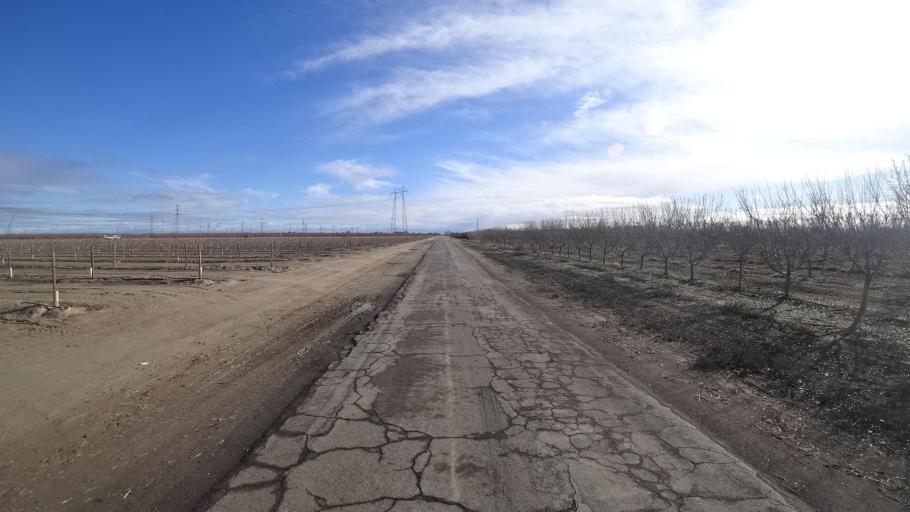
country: US
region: California
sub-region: Kern County
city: Shafter
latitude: 35.3836
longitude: -119.2761
